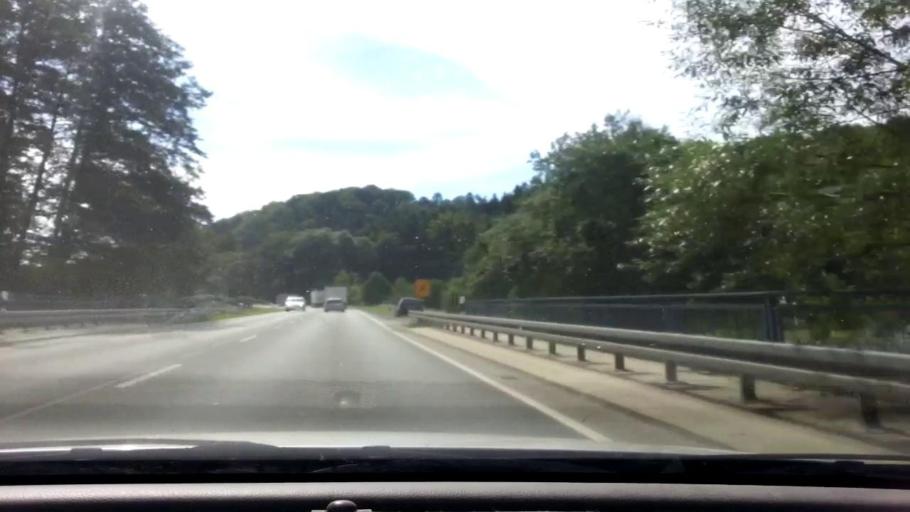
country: DE
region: Bavaria
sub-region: Upper Franconia
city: Bad Berneck im Fichtelgebirge
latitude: 50.0418
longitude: 11.6697
